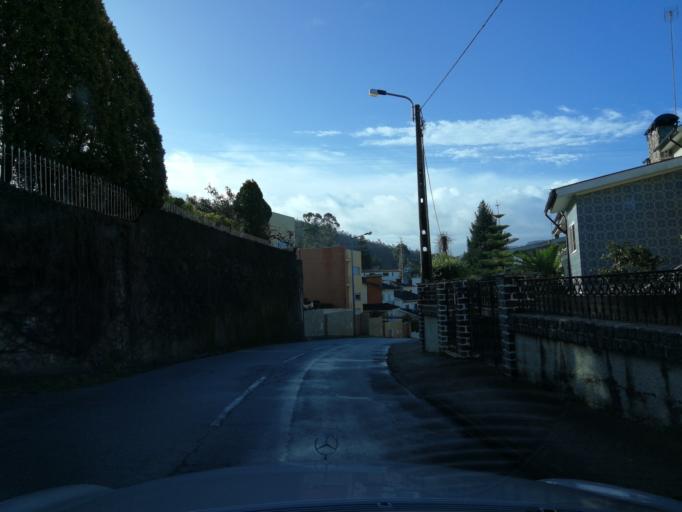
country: PT
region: Braga
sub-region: Braga
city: Braga
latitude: 41.5470
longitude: -8.3893
